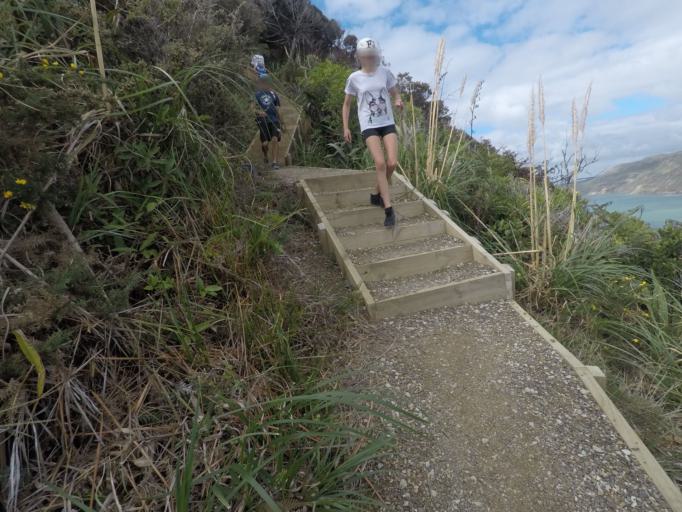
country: NZ
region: Auckland
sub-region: Auckland
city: Titirangi
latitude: -37.0361
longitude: 174.5171
